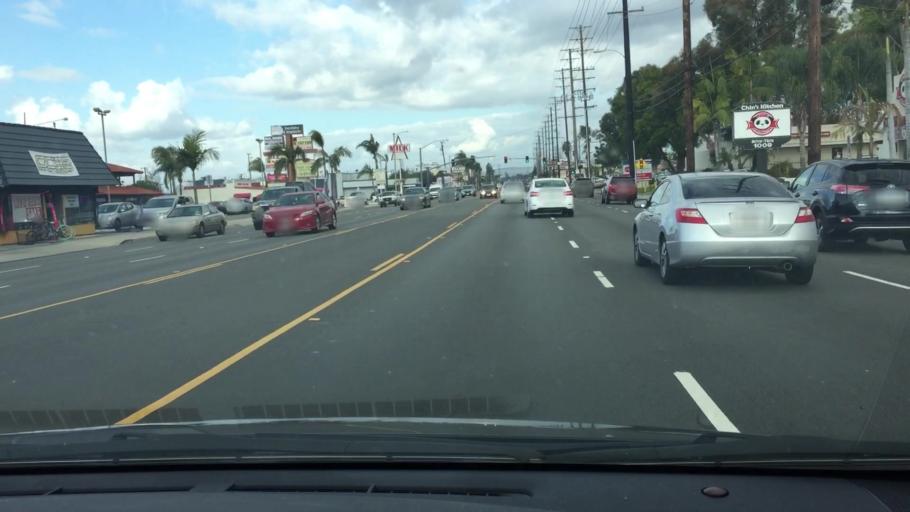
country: US
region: California
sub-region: Orange County
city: Orange
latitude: 33.8040
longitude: -117.8357
